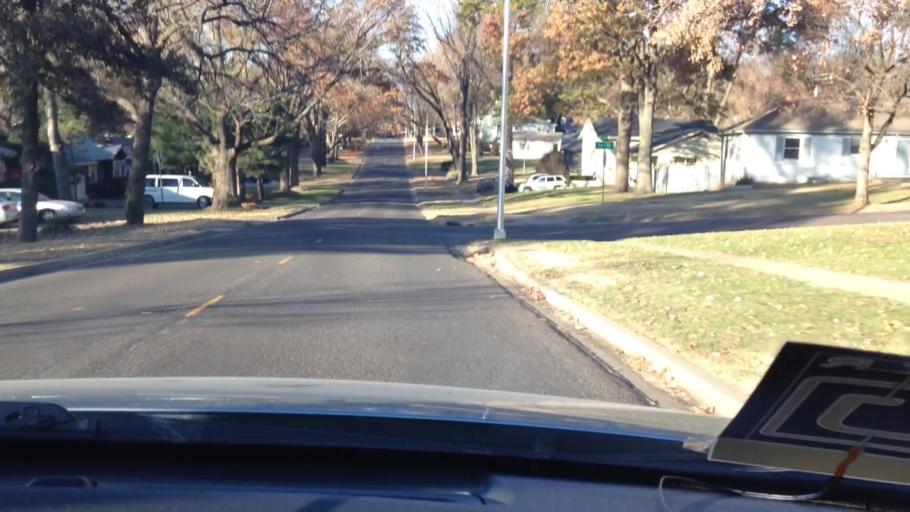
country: US
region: Kansas
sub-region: Johnson County
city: Overland Park
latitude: 38.9728
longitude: -94.6583
